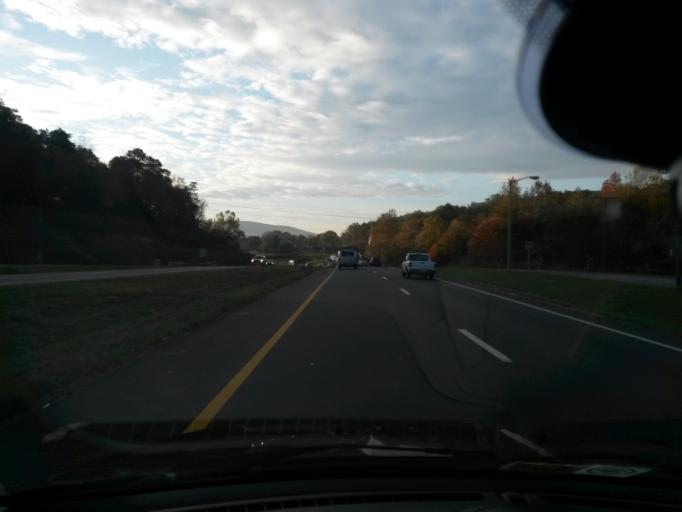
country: US
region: Virginia
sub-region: Botetourt County
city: Cloverdale
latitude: 37.3481
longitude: -79.8829
